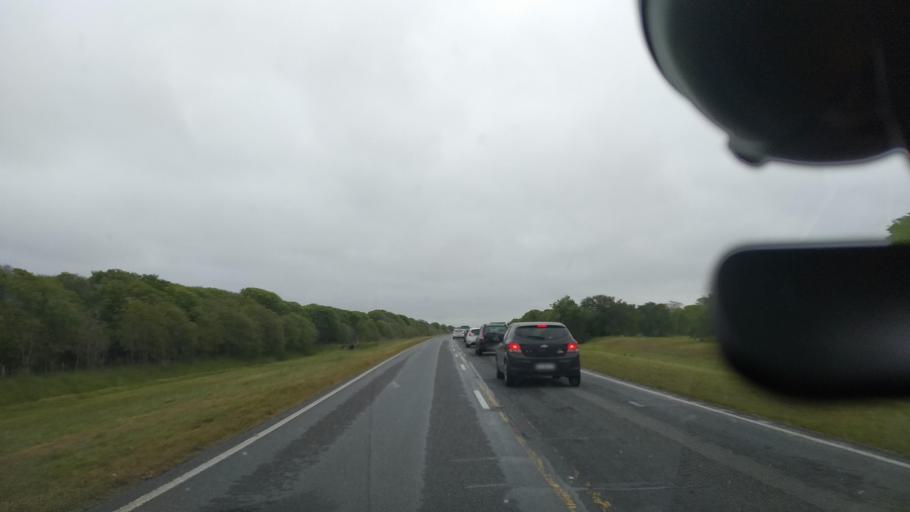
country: AR
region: Buenos Aires
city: Veronica
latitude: -35.7896
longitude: -57.4028
